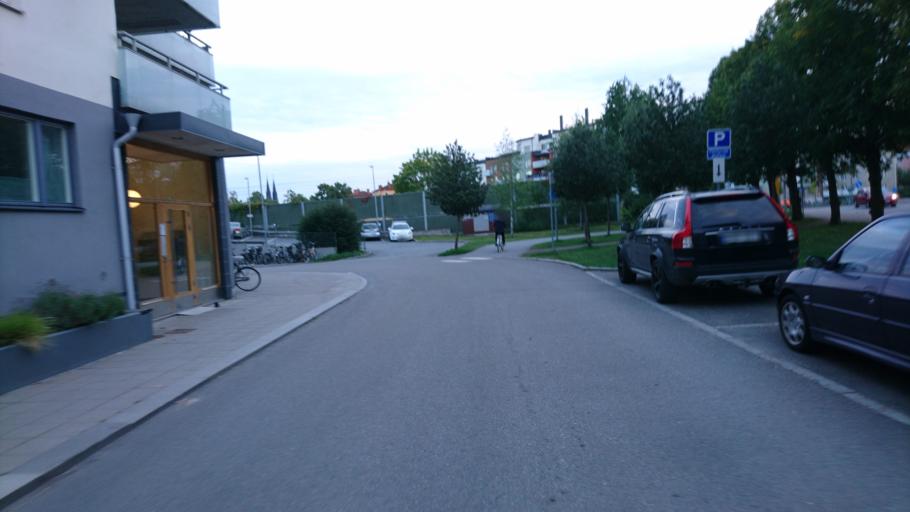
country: SE
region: Uppsala
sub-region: Uppsala Kommun
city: Uppsala
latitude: 59.8671
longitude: 17.6228
